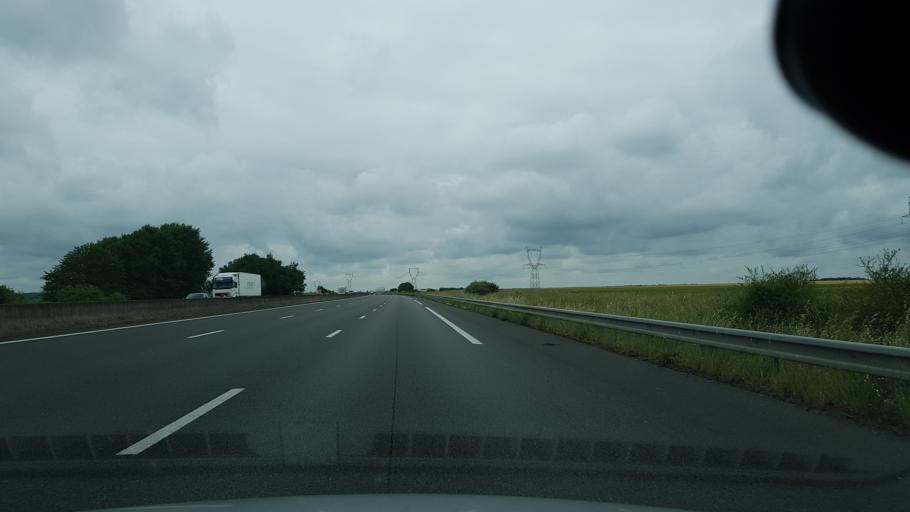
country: FR
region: Centre
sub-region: Departement du Loir-et-Cher
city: Herbault
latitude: 47.6169
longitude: 1.1879
